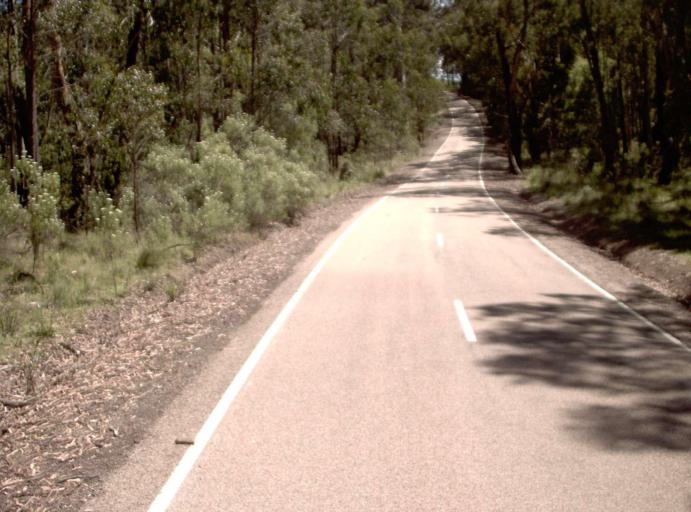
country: AU
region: Victoria
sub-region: East Gippsland
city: Lakes Entrance
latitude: -37.2845
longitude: 148.2557
